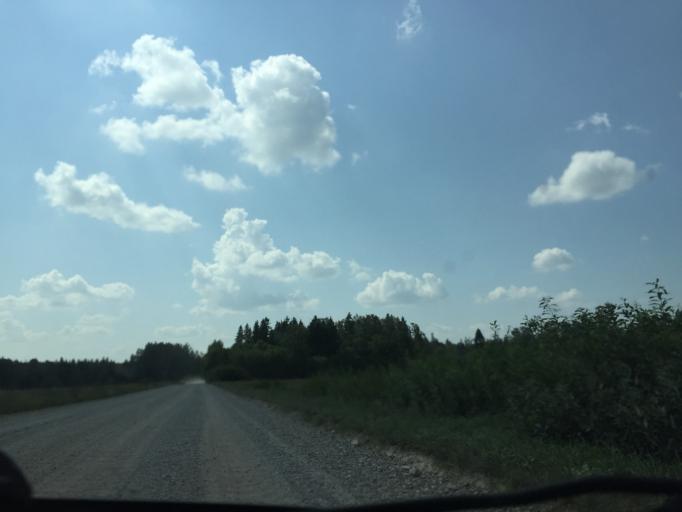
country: LV
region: Tervete
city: Zelmeni
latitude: 56.4004
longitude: 23.3227
